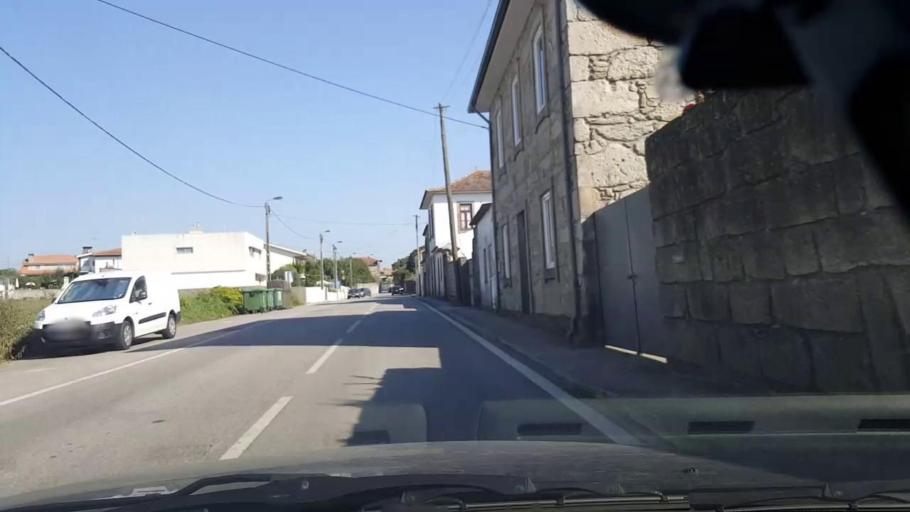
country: PT
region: Porto
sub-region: Maia
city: Gemunde
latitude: 41.3024
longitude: -8.6791
